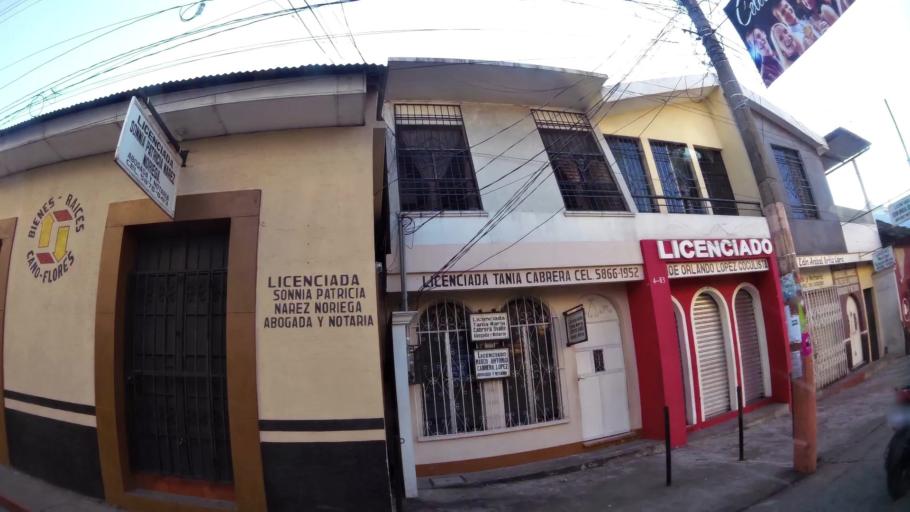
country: GT
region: Suchitepeque
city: Mazatenango
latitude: 14.5353
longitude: -91.5027
